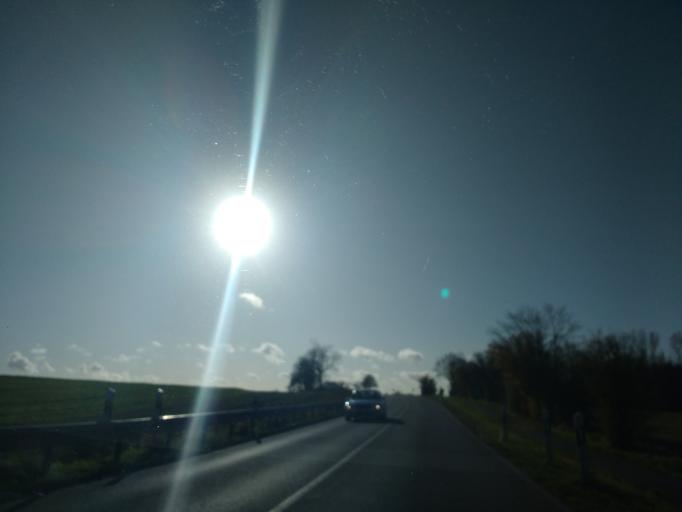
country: DE
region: Mecklenburg-Vorpommern
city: Ostseebad Boltenhagen
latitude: 53.9778
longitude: 11.1824
